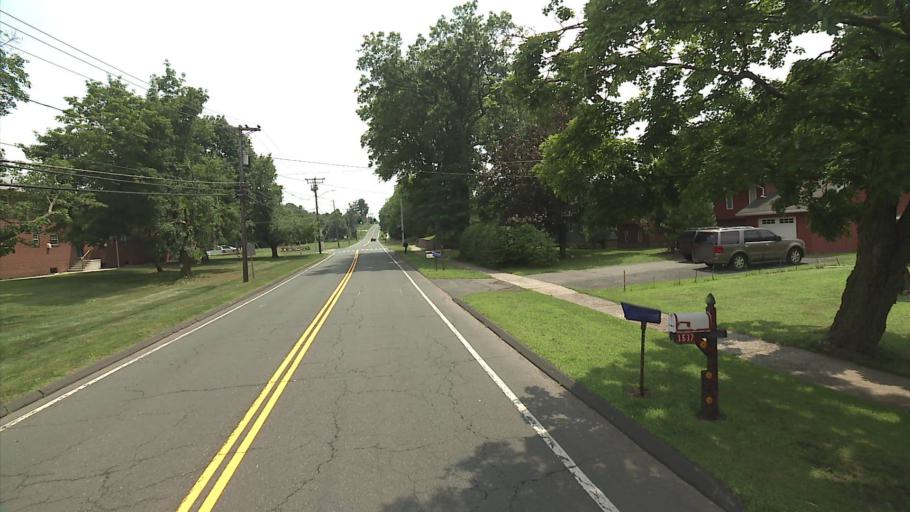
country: US
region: Connecticut
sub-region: Hartford County
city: Newington
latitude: 41.6695
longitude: -72.7280
